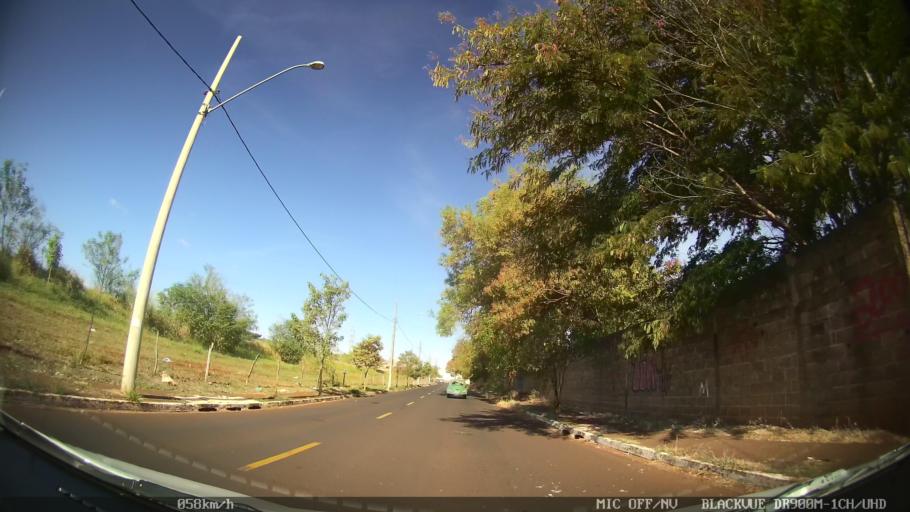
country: BR
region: Sao Paulo
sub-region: Ribeirao Preto
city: Ribeirao Preto
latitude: -21.1751
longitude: -47.7799
